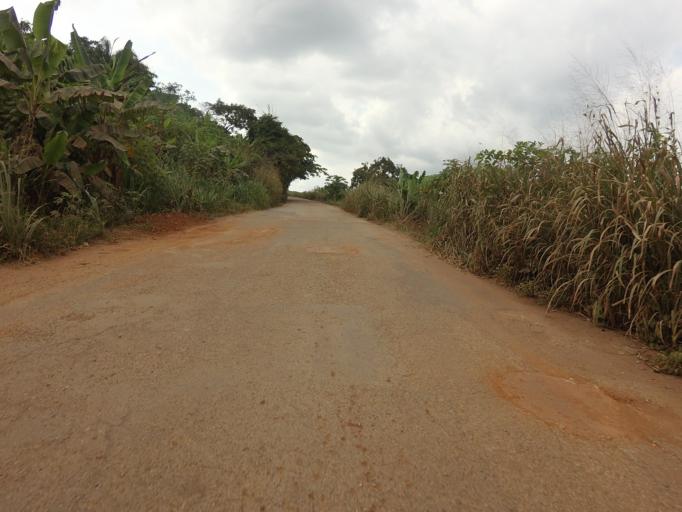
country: GH
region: Volta
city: Ho
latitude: 6.6800
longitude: 0.3490
